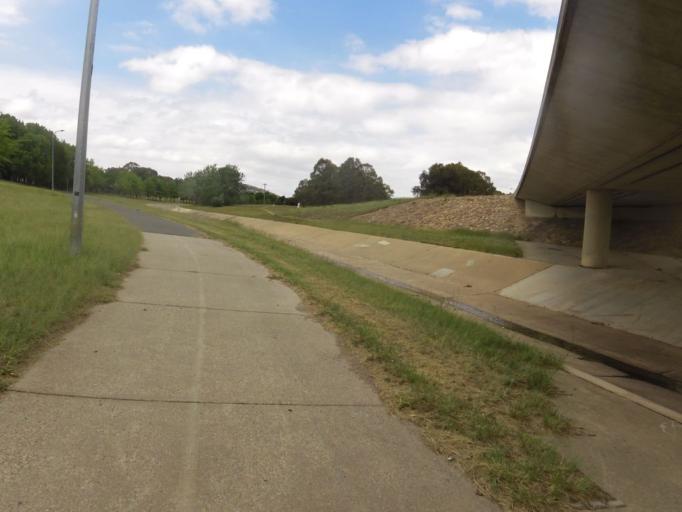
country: AU
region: Australian Capital Territory
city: Macarthur
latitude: -35.4207
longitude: 149.1050
